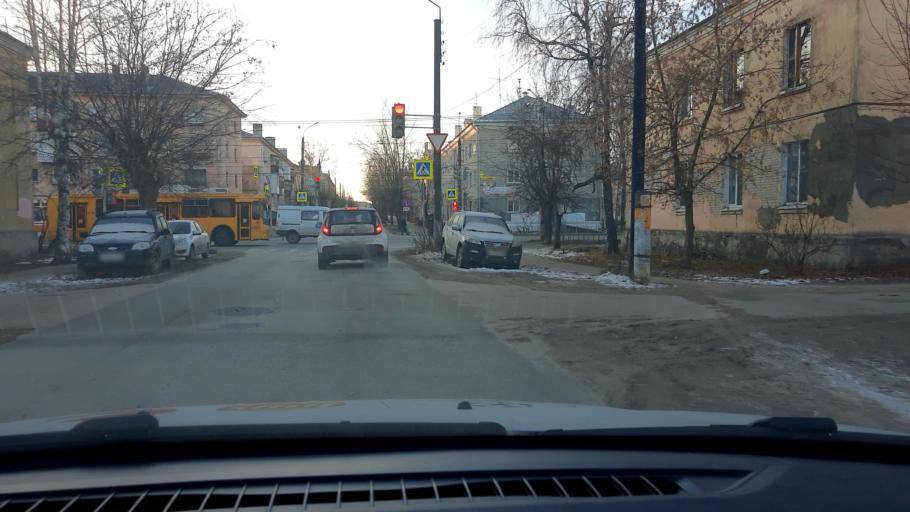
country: RU
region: Nizjnij Novgorod
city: Dzerzhinsk
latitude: 56.2496
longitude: 43.4571
